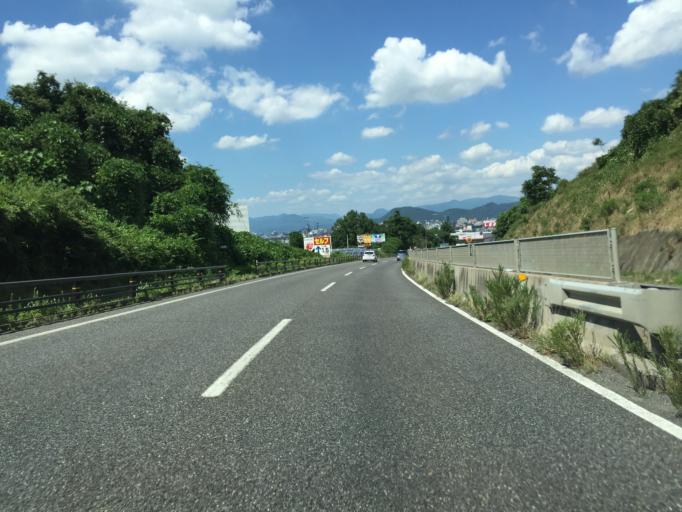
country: JP
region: Fukushima
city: Fukushima-shi
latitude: 37.7182
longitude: 140.4652
